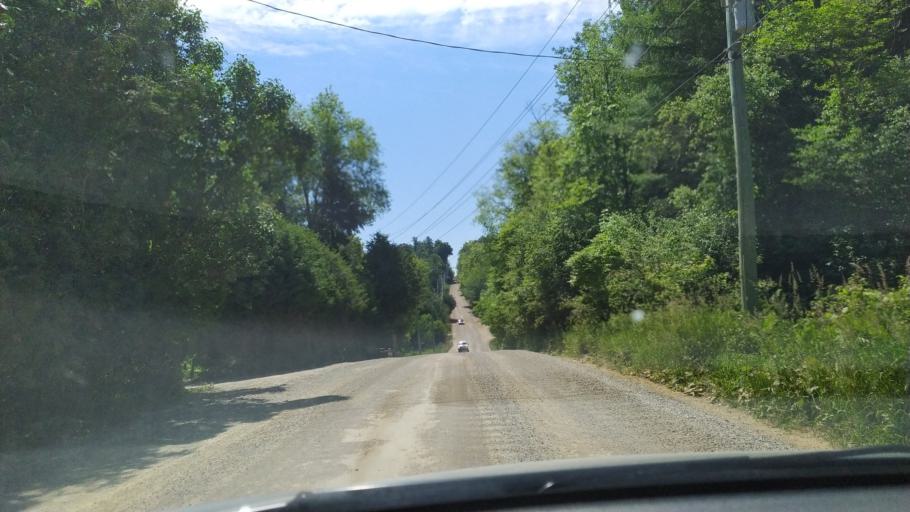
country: CA
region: Ontario
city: Waterloo
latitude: 43.4673
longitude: -80.6122
